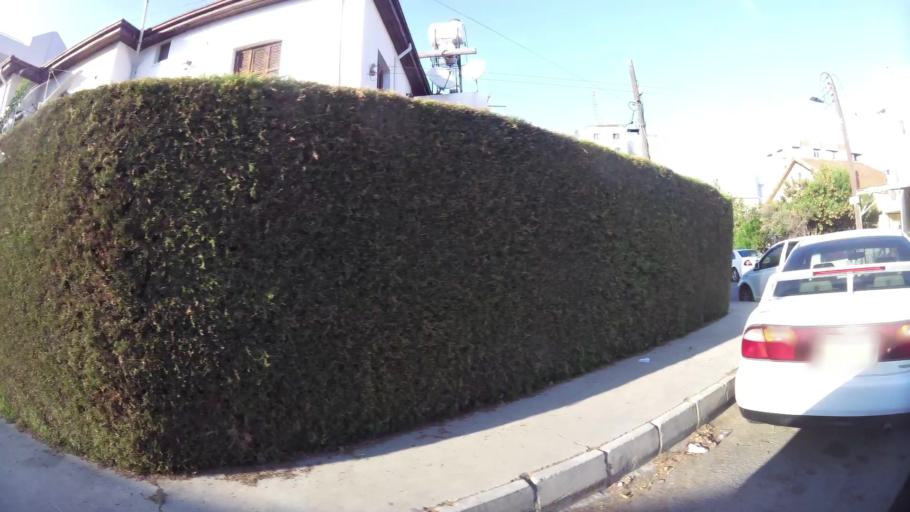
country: CY
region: Lefkosia
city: Nicosia
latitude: 35.1873
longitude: 33.3649
